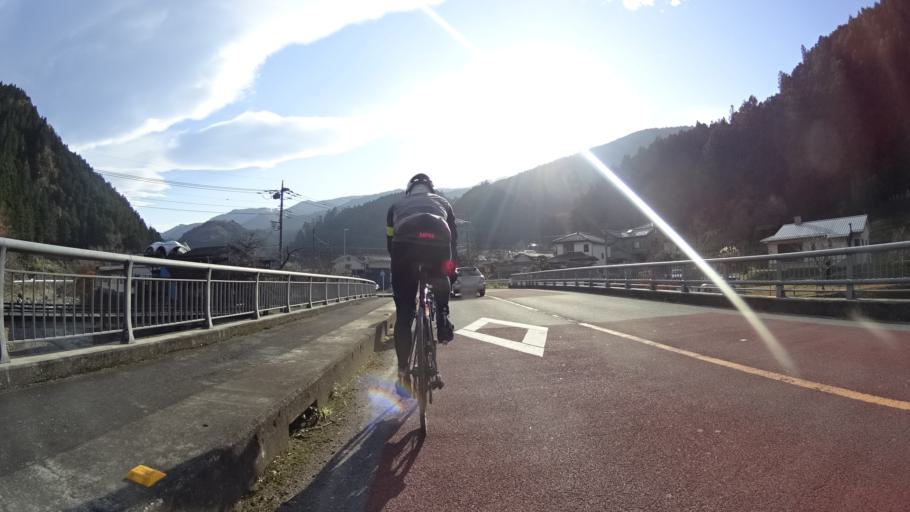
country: JP
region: Tokyo
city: Ome
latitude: 35.8661
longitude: 139.1870
